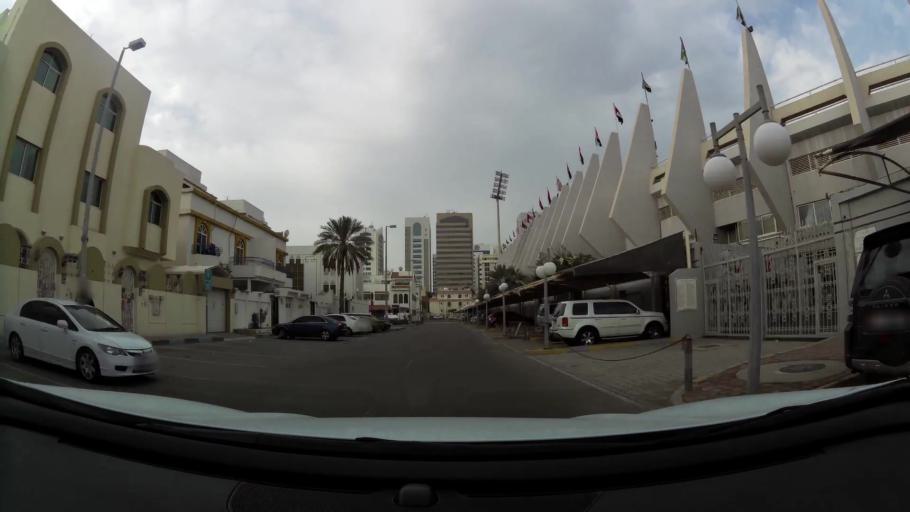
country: AE
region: Abu Dhabi
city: Abu Dhabi
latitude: 24.4692
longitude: 54.3764
